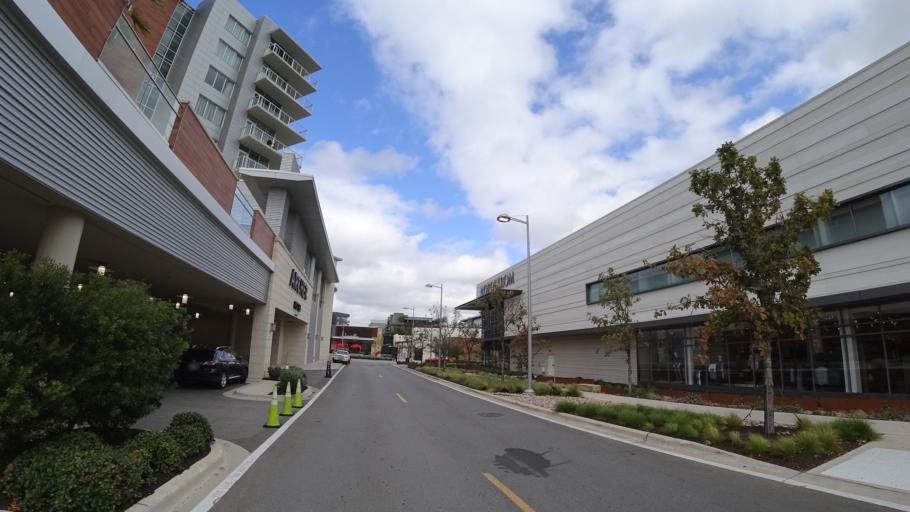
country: US
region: Texas
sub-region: Travis County
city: Wells Branch
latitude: 30.4020
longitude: -97.7209
